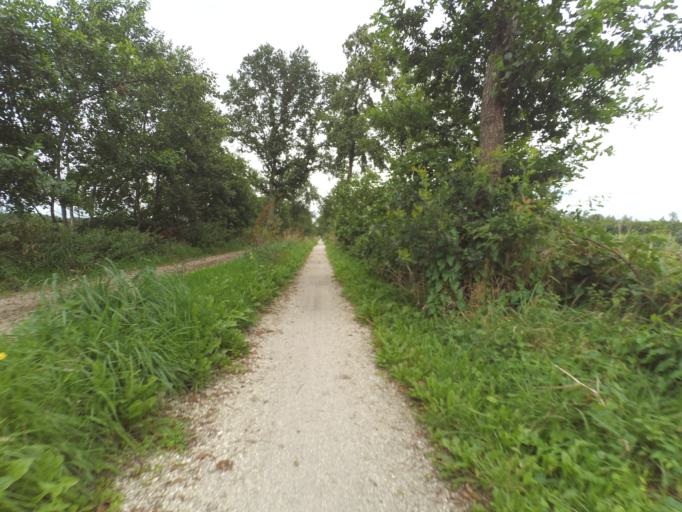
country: NL
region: Friesland
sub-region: Gemeente Kollumerland en Nieuwkruisland
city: Kollum
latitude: 53.2814
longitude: 6.1272
